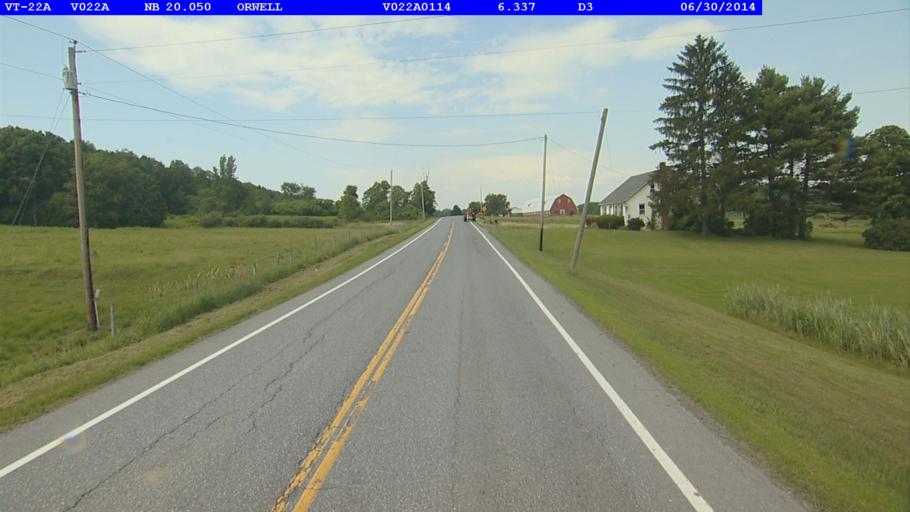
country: US
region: New York
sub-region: Essex County
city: Ticonderoga
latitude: 43.8480
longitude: -73.3094
